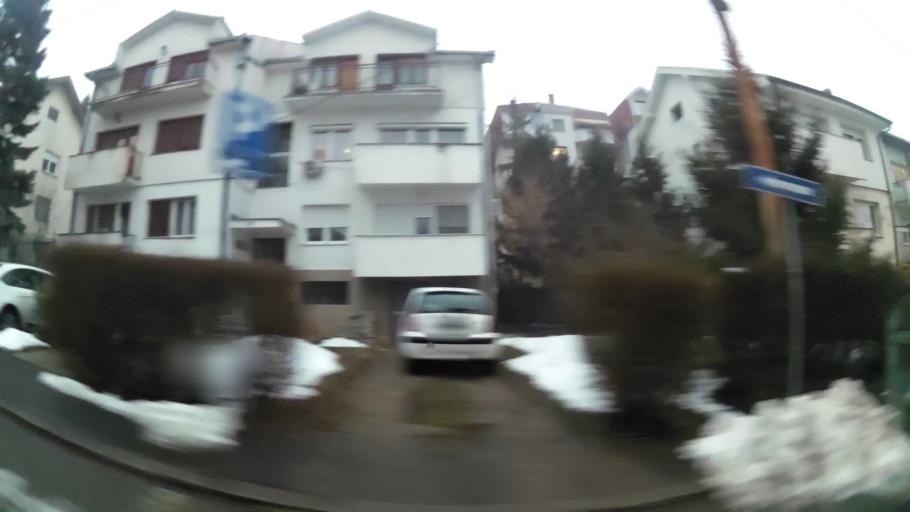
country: RS
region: Central Serbia
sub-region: Belgrade
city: Rakovica
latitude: 44.7560
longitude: 20.4259
